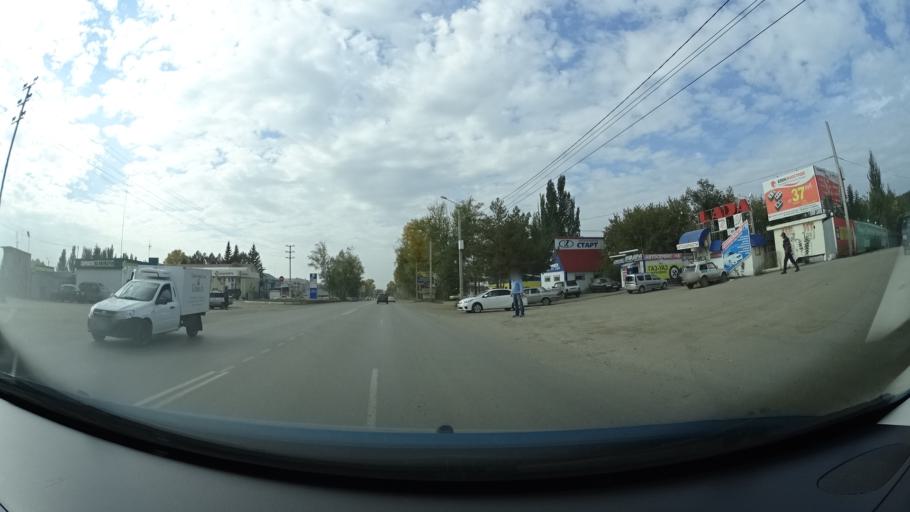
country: RU
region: Bashkortostan
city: Oktyabr'skiy
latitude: 54.4918
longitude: 53.4662
